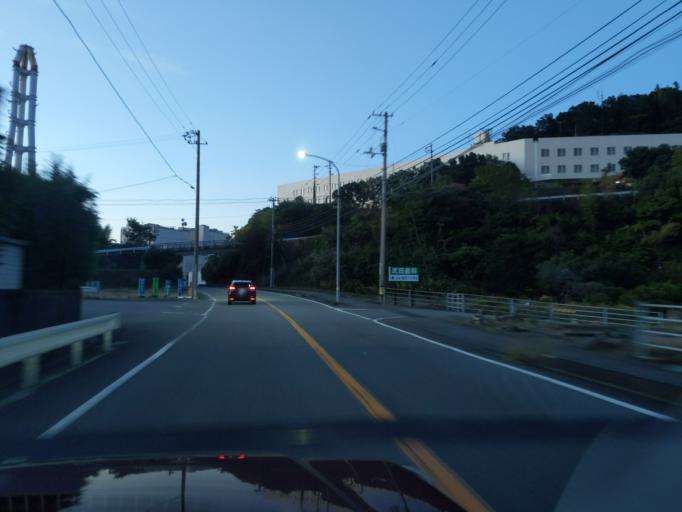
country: JP
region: Tokushima
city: Anan
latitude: 33.8827
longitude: 134.6526
